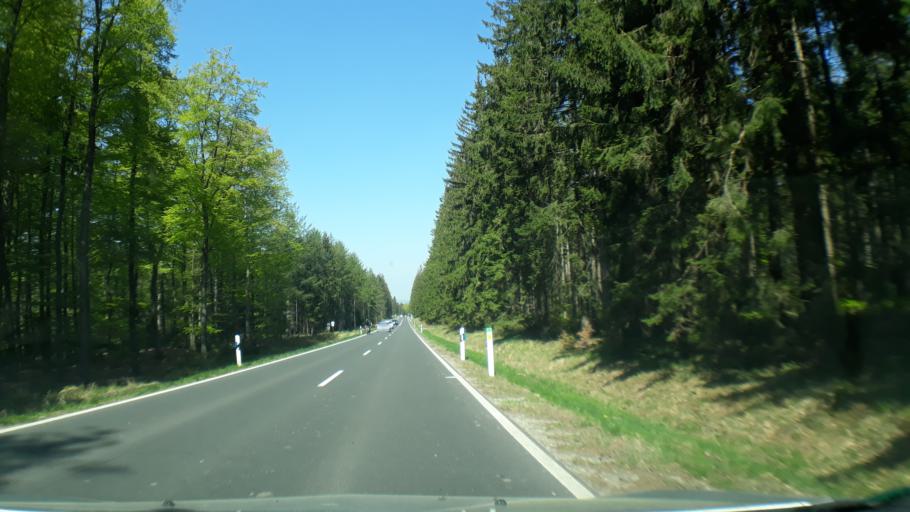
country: DE
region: North Rhine-Westphalia
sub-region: Regierungsbezirk Koln
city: Roetgen
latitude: 50.6616
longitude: 6.2477
